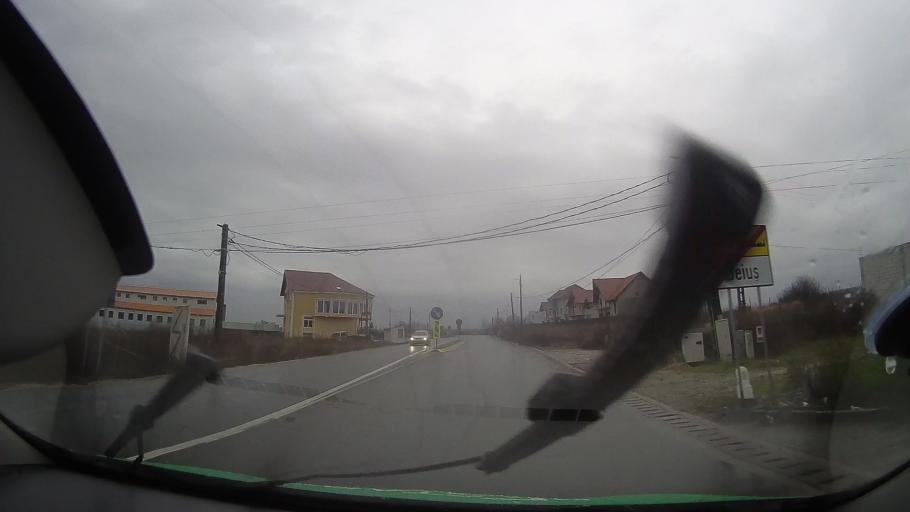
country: RO
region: Bihor
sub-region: Municipiul Beius
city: Beius
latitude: 46.6695
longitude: 22.3360
